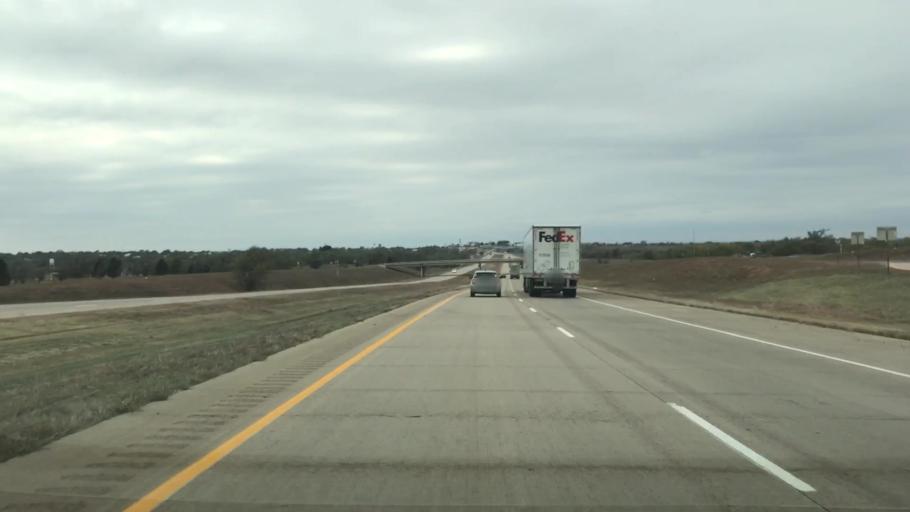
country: US
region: Texas
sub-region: Wheeler County
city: Shamrock
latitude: 35.2273
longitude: -100.2224
